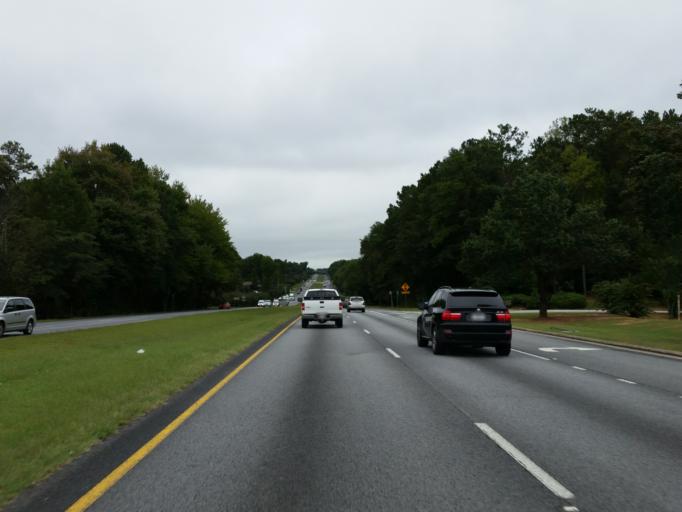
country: US
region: Georgia
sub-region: Clayton County
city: Jonesboro
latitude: 33.5081
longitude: -84.3557
